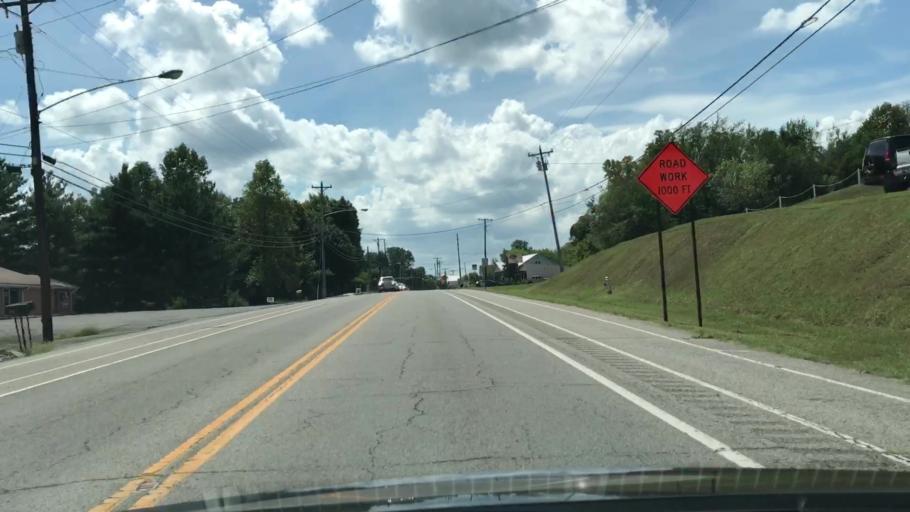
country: US
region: Tennessee
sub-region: Sumner County
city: White House
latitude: 36.4727
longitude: -86.6505
